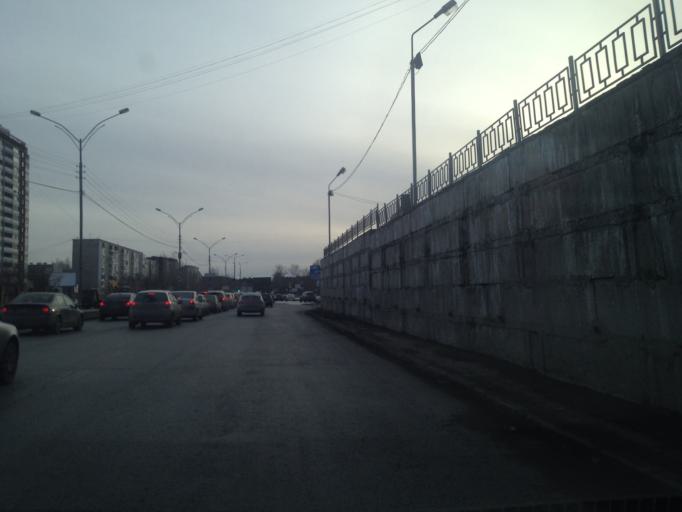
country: RU
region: Sverdlovsk
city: Sovkhoznyy
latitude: 56.8120
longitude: 60.5483
